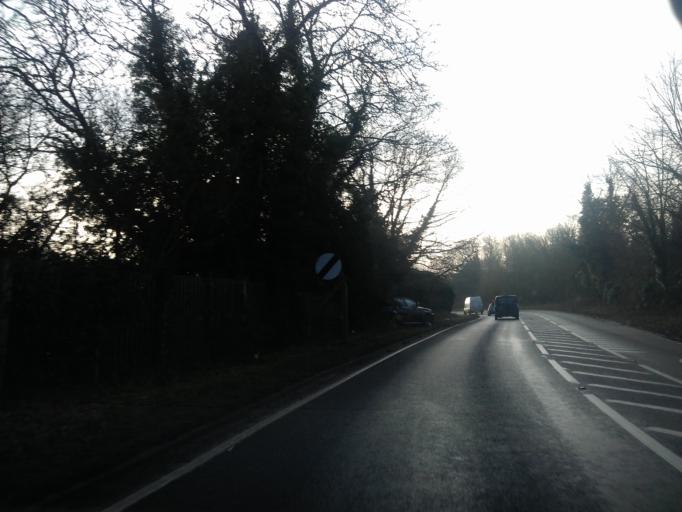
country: GB
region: England
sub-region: Essex
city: Alresford
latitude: 51.8517
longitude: 1.0110
